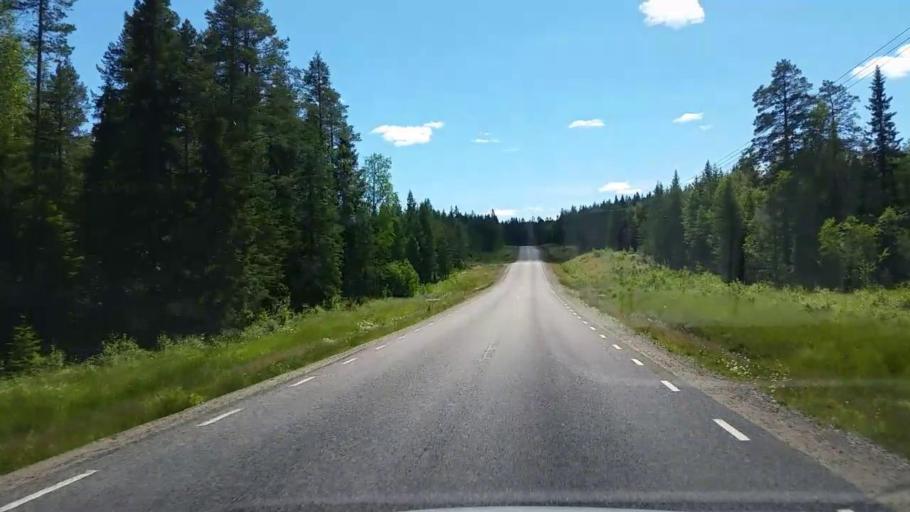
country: SE
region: Gaevleborg
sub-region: Ovanakers Kommun
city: Edsbyn
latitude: 61.5346
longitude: 15.6800
